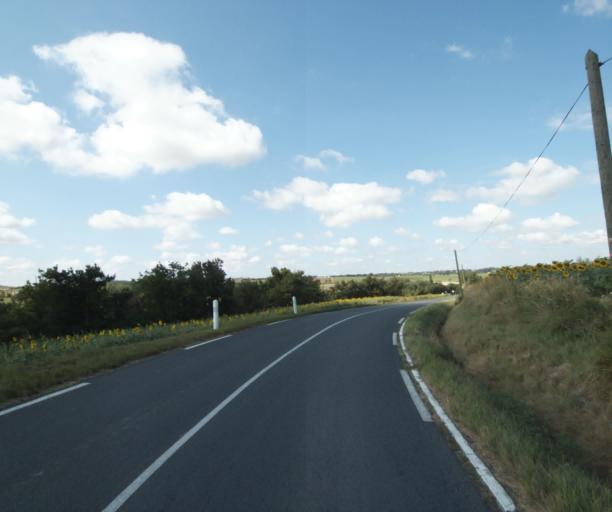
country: FR
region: Midi-Pyrenees
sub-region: Departement de la Haute-Garonne
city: Saint-Felix-Lauragais
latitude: 43.4466
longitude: 1.8124
